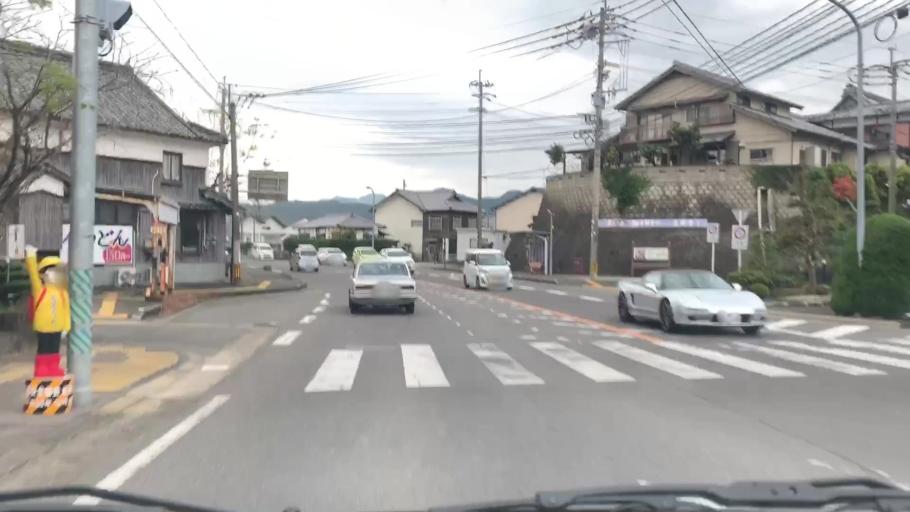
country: JP
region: Saga Prefecture
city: Kashima
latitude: 33.1323
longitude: 130.0614
